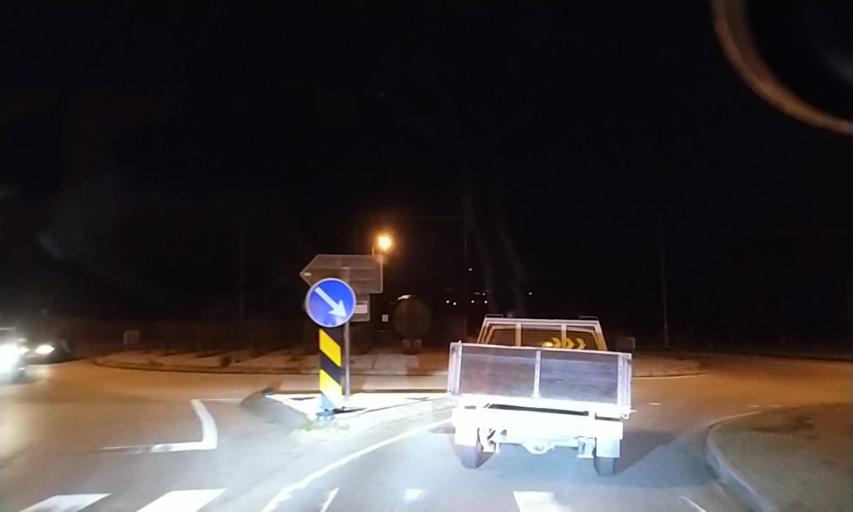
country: PT
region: Vila Real
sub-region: Sabrosa
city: Sabrosa
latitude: 41.2651
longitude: -7.4920
